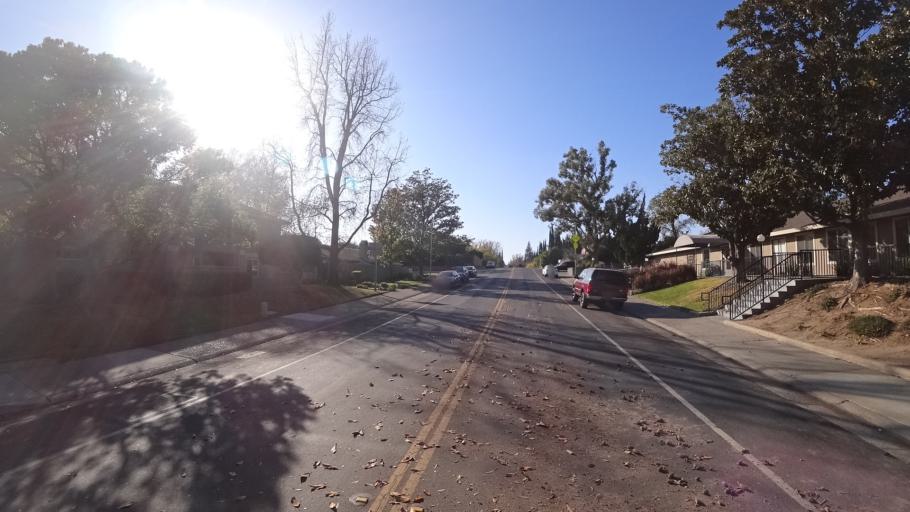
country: US
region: California
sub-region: Sacramento County
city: Fair Oaks
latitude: 38.6733
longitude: -121.2765
